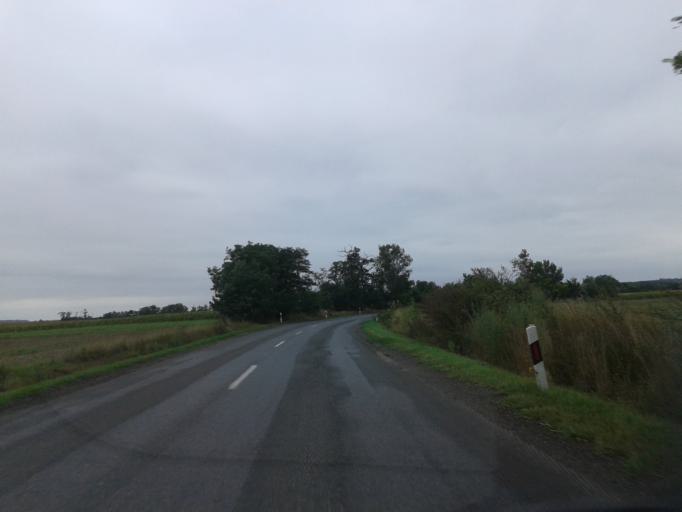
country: HU
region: Bacs-Kiskun
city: Szalkszentmarton
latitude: 46.9661
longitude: 18.9841
